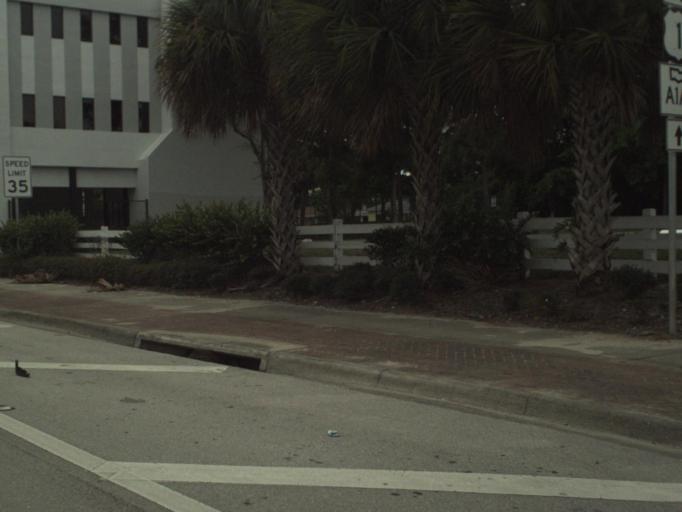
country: US
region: Florida
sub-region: Palm Beach County
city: Lake Clarke Shores
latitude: 26.6759
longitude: -80.0653
